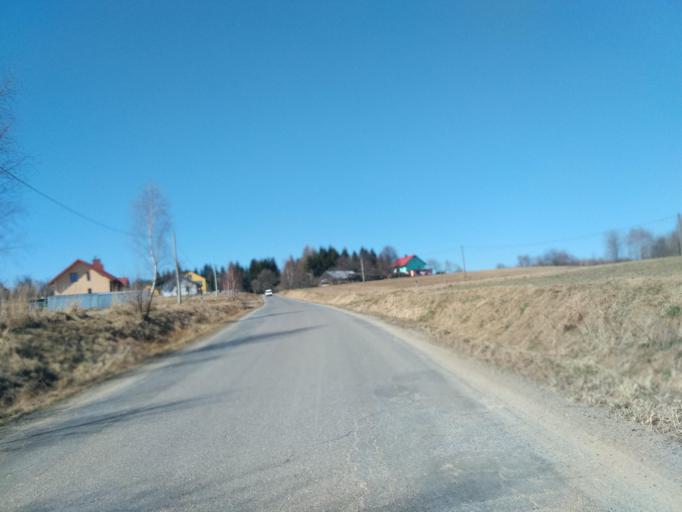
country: PL
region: Subcarpathian Voivodeship
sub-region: Powiat debicki
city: Brzostek
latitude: 49.9563
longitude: 21.4296
